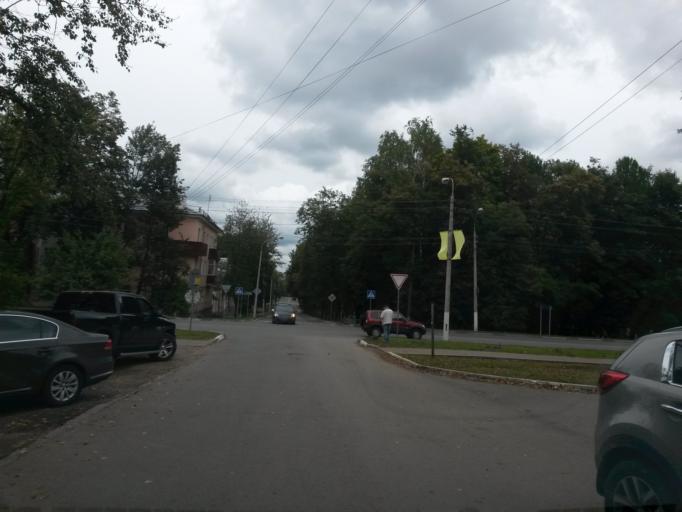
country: RU
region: Moskovskaya
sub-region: Chekhovskiy Rayon
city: Chekhov
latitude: 55.1458
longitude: 37.4791
